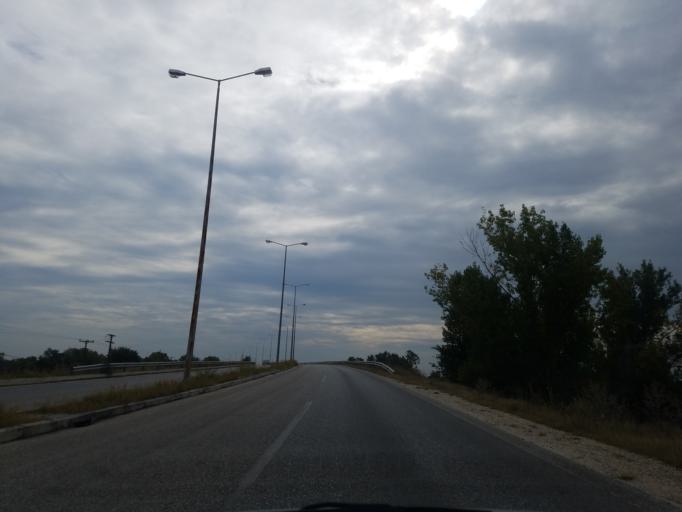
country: GR
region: Thessaly
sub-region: Trikala
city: Pyrgetos
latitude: 39.5215
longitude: 21.7541
